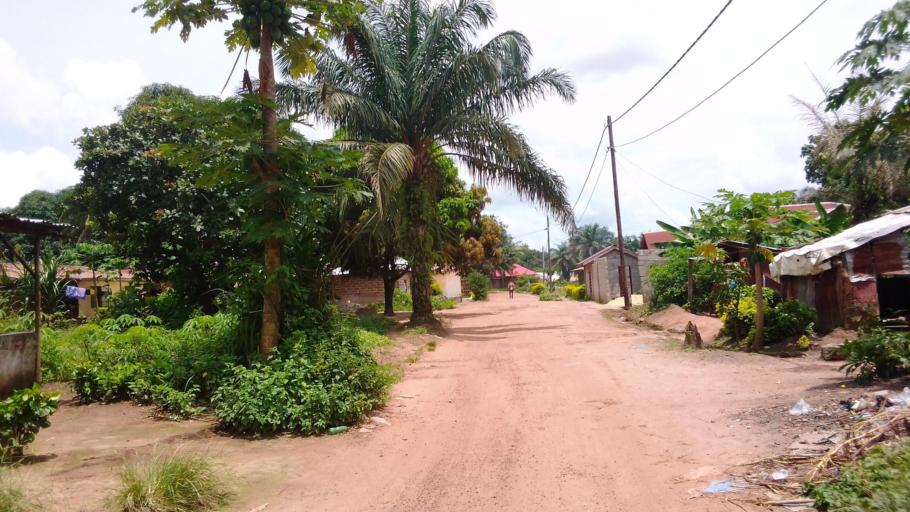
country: SL
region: Northern Province
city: Makeni
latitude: 8.8706
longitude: -12.0374
